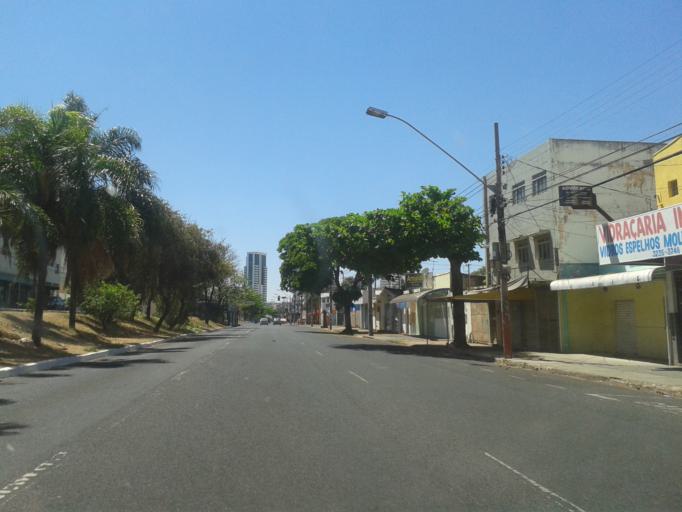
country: BR
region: Minas Gerais
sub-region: Uberlandia
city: Uberlandia
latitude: -18.9150
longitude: -48.2687
